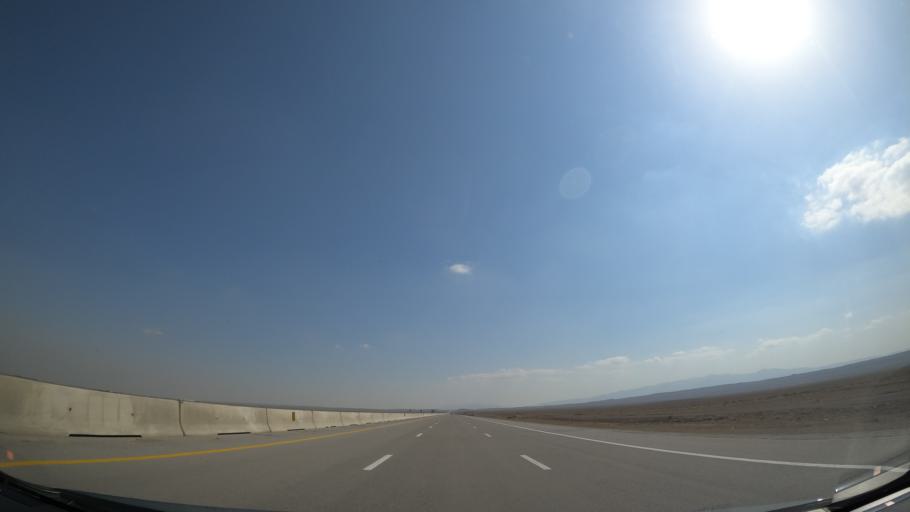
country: IR
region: Alborz
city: Nazarabad
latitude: 35.8309
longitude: 50.5000
